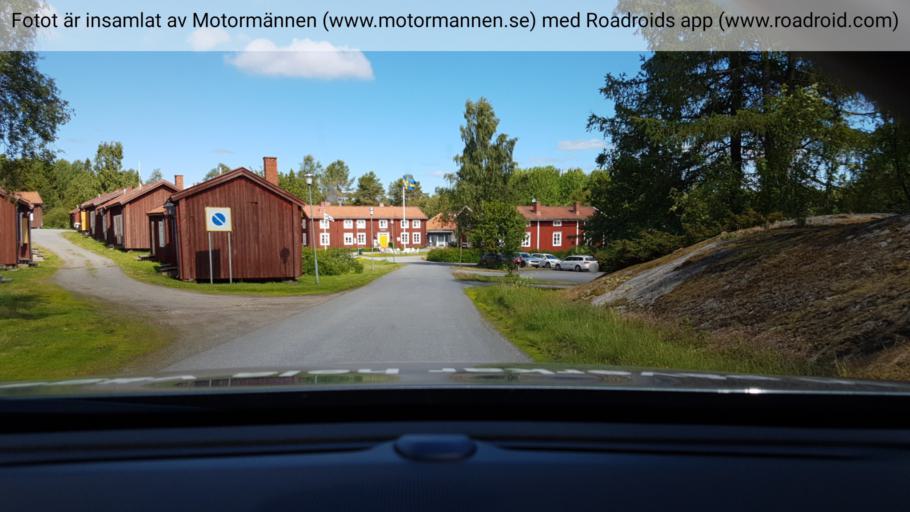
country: SE
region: Vaesterbotten
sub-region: Skelleftea Kommun
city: Burea
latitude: 64.3689
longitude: 21.3180
